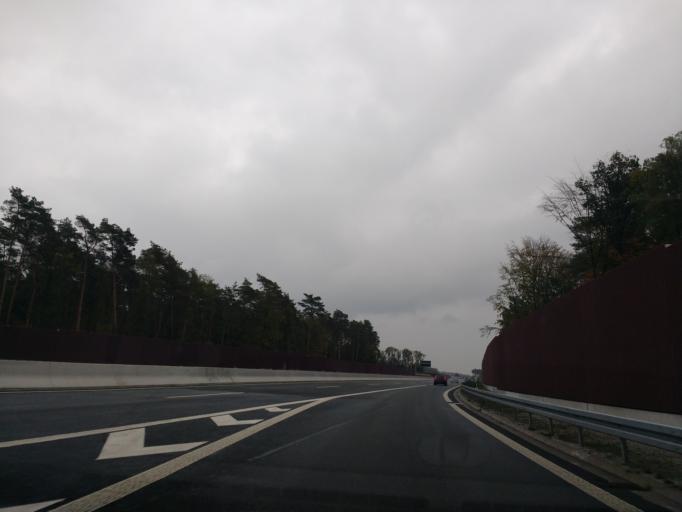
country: DE
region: North Rhine-Westphalia
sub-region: Regierungsbezirk Detmold
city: Steinhagen
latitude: 52.0212
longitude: 8.3859
